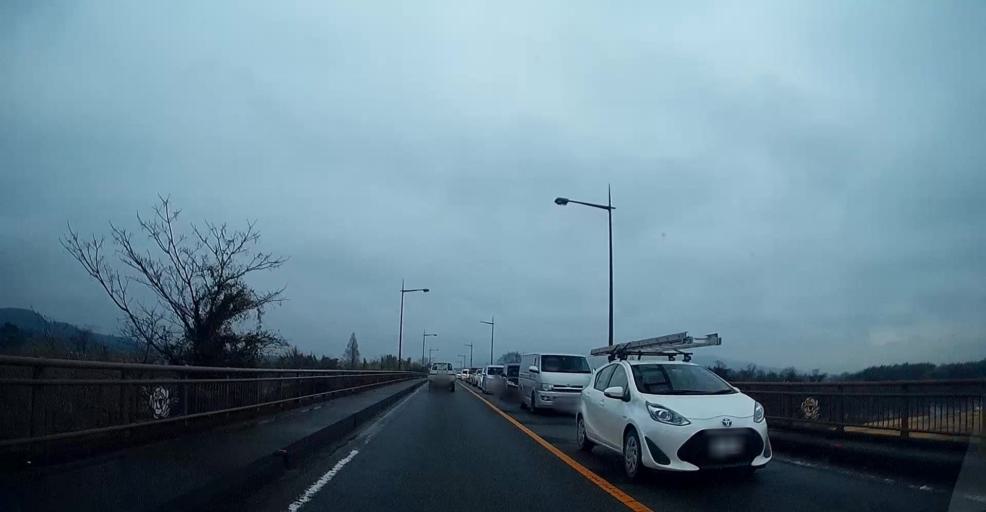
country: JP
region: Kumamoto
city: Kumamoto
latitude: 32.7363
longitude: 130.7396
